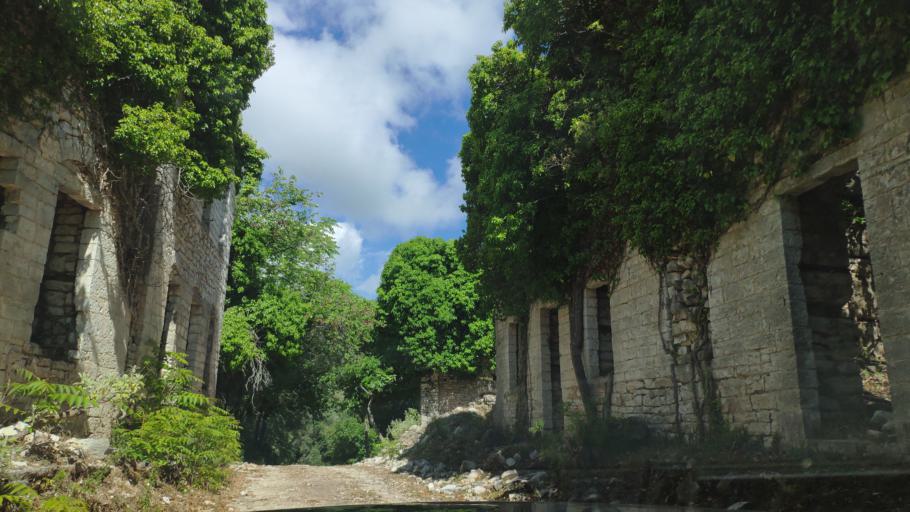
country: AL
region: Vlore
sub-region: Rrethi i Sarandes
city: Konispol
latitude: 39.6375
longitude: 20.2020
